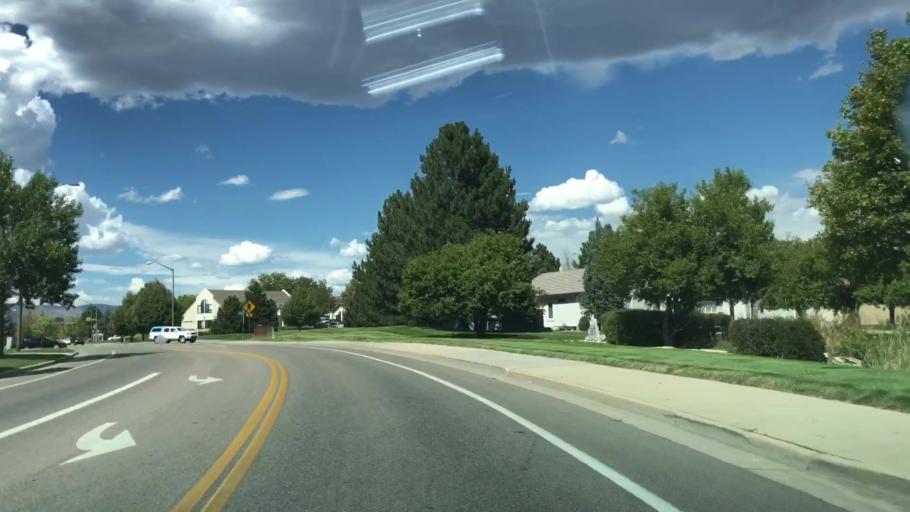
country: US
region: Colorado
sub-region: Larimer County
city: Fort Collins
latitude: 40.5313
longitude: -105.0716
